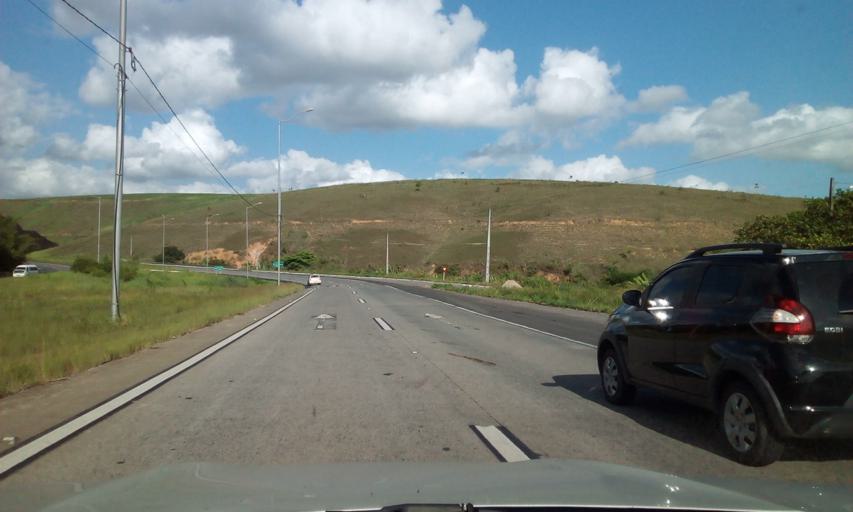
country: BR
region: Pernambuco
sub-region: Palmares
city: Palmares
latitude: -8.6626
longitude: -35.5670
